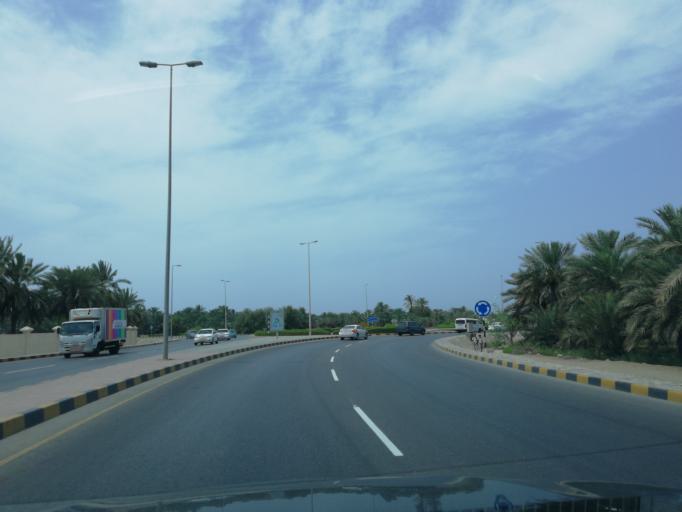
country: OM
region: Muhafazat Masqat
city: As Sib al Jadidah
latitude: 23.6781
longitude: 58.1384
